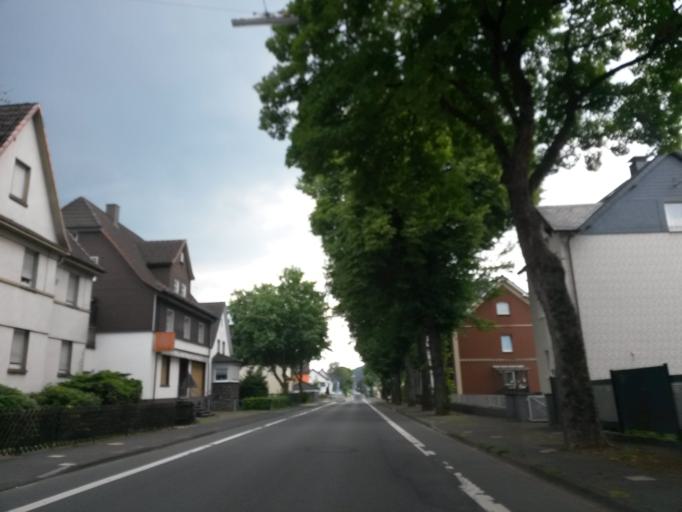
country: DE
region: North Rhine-Westphalia
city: Kreuztal
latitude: 50.9449
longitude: 7.9995
